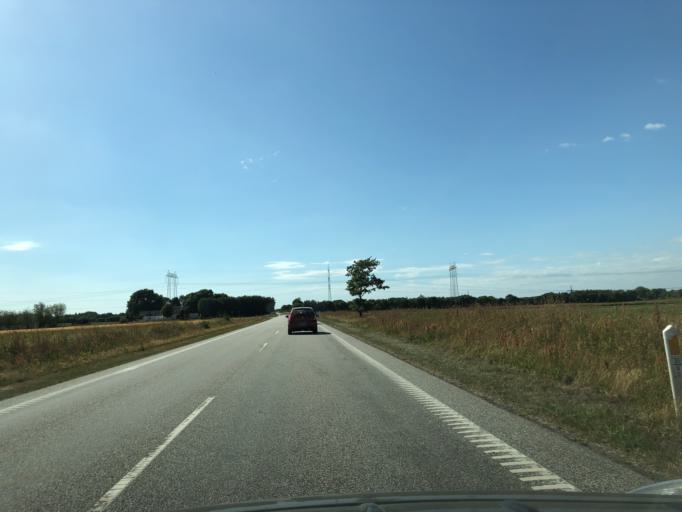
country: DK
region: North Denmark
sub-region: Vesthimmerland Kommune
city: Alestrup
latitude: 56.6202
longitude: 9.5885
